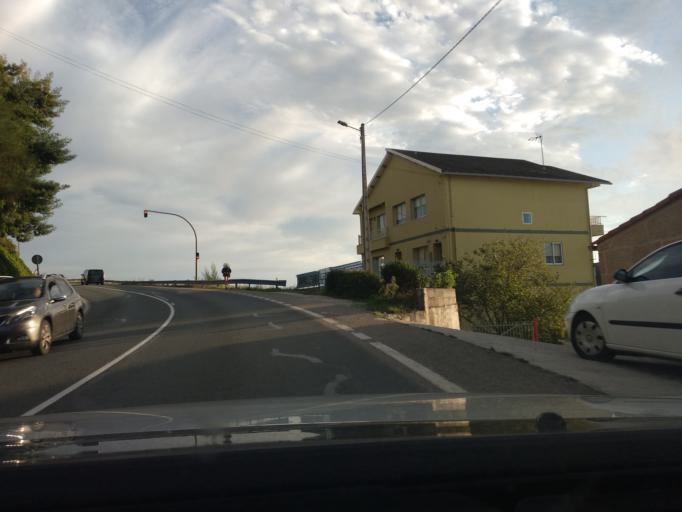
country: ES
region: Galicia
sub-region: Provincia de Pontevedra
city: Moana
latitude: 42.2834
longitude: -8.7136
